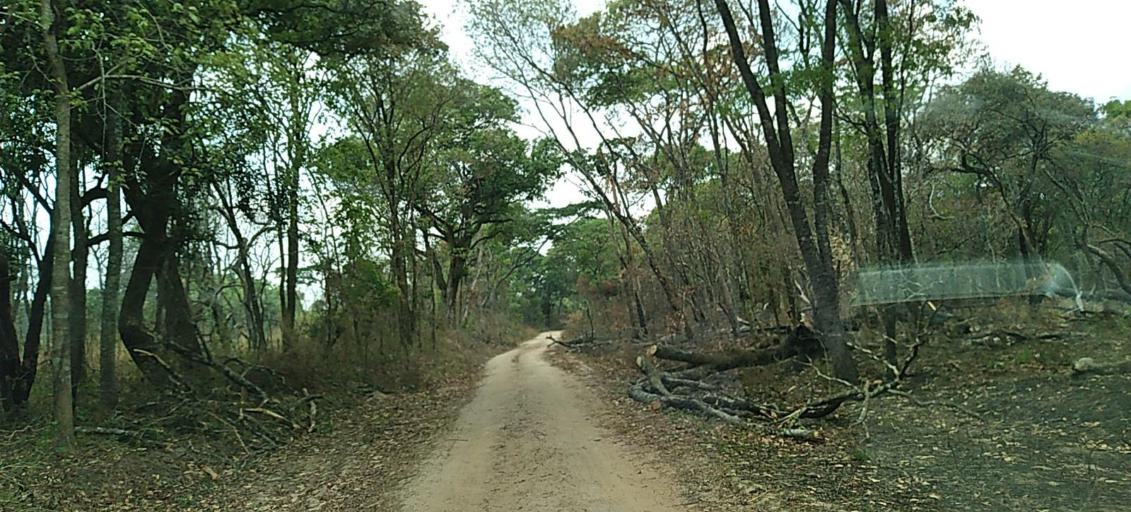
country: ZM
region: Copperbelt
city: Chingola
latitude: -12.7554
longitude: 27.7088
